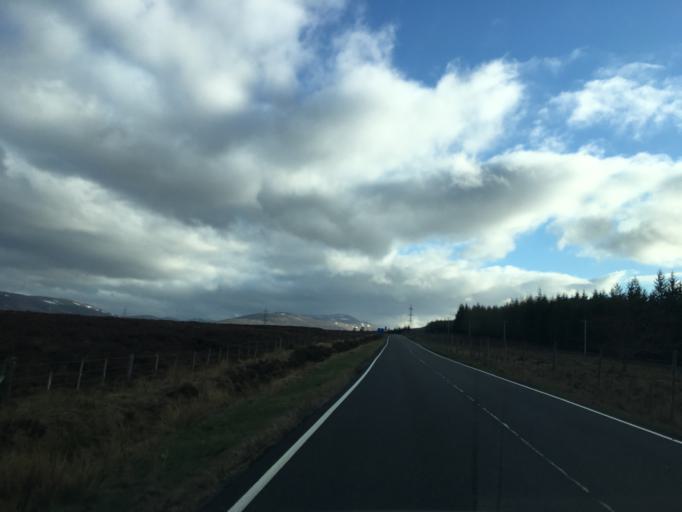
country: GB
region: Scotland
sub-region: Highland
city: Kingussie
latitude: 56.9701
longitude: -4.2369
